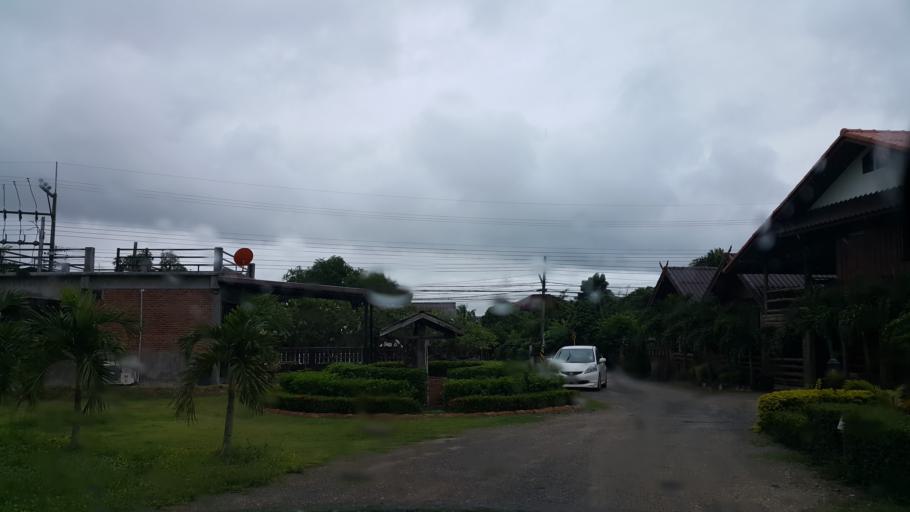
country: TH
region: Phayao
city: Chiang Kham
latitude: 19.5352
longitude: 100.2947
